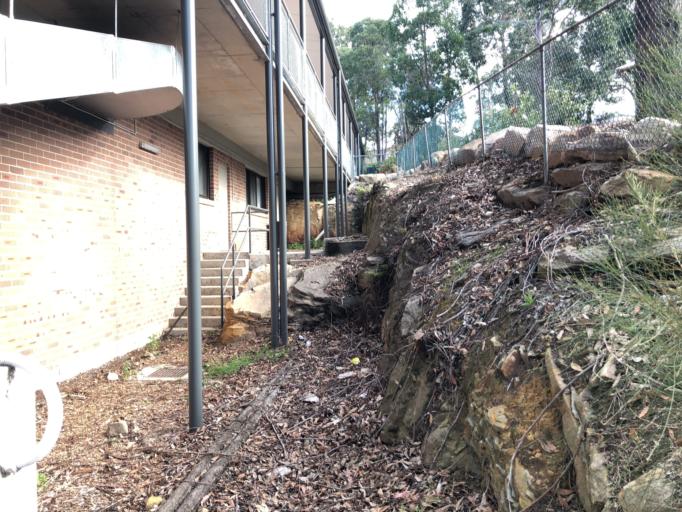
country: AU
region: New South Wales
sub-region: The Hills Shire
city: Glenhaven
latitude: -33.6833
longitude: 151.0131
